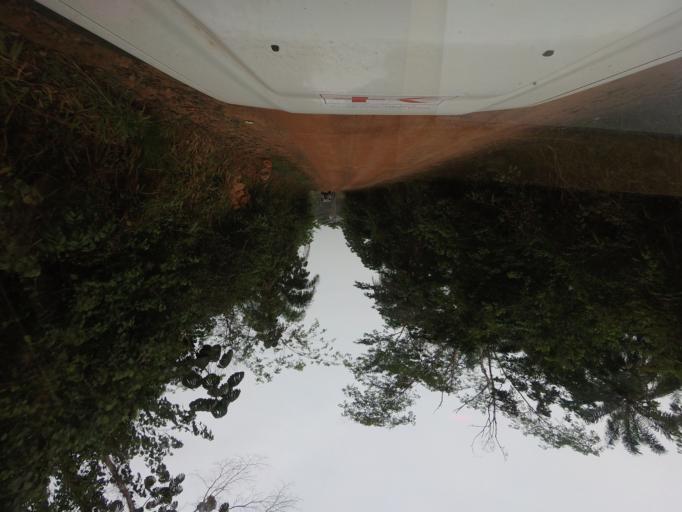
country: LR
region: Lofa
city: Voinjama
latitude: 8.3891
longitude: -9.8136
